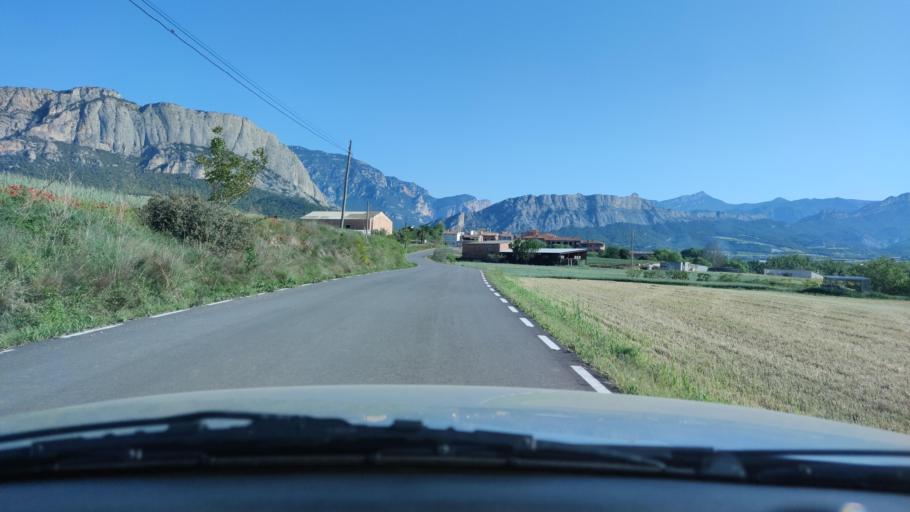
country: ES
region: Catalonia
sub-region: Provincia de Lleida
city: Oliana
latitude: 42.0575
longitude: 1.2957
